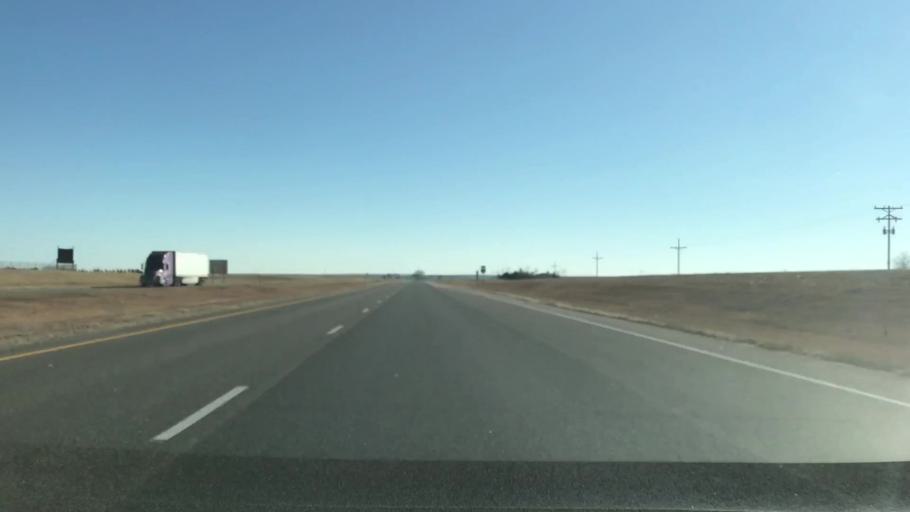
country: US
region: Colorado
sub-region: Lincoln County
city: Hugo
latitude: 39.2850
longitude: -103.0548
